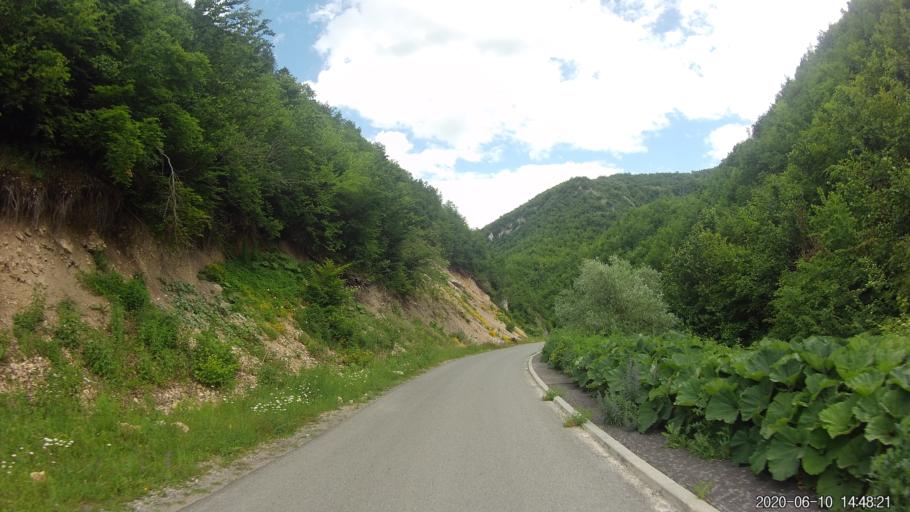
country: XK
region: Prizren
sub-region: Komuna e Therandes
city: Budakovo
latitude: 42.3914
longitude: 20.9626
